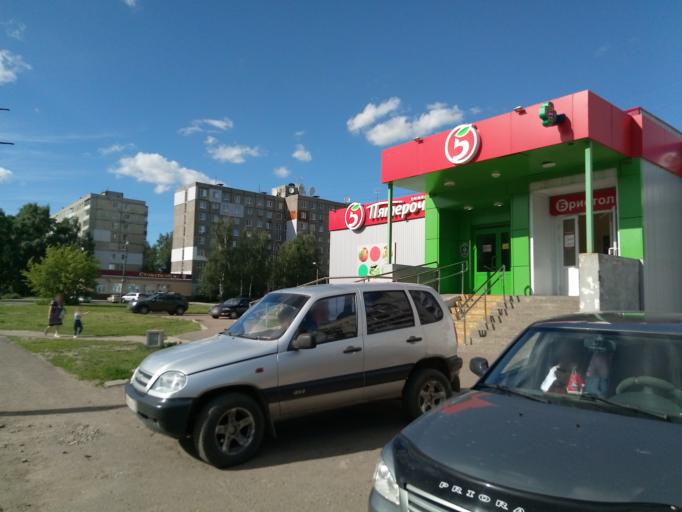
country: RU
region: Jaroslavl
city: Yaroslavl
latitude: 57.6425
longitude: 39.9446
